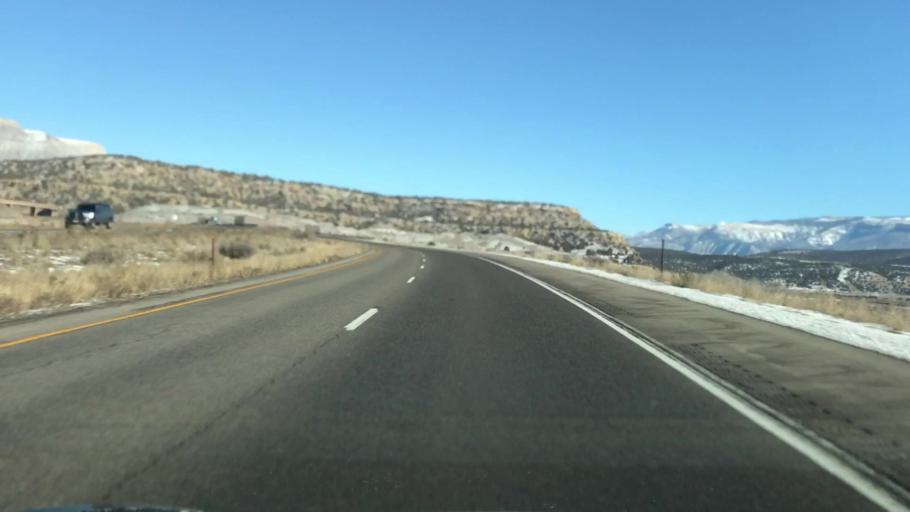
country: US
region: Colorado
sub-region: Garfield County
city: Parachute
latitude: 39.3530
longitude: -108.1737
